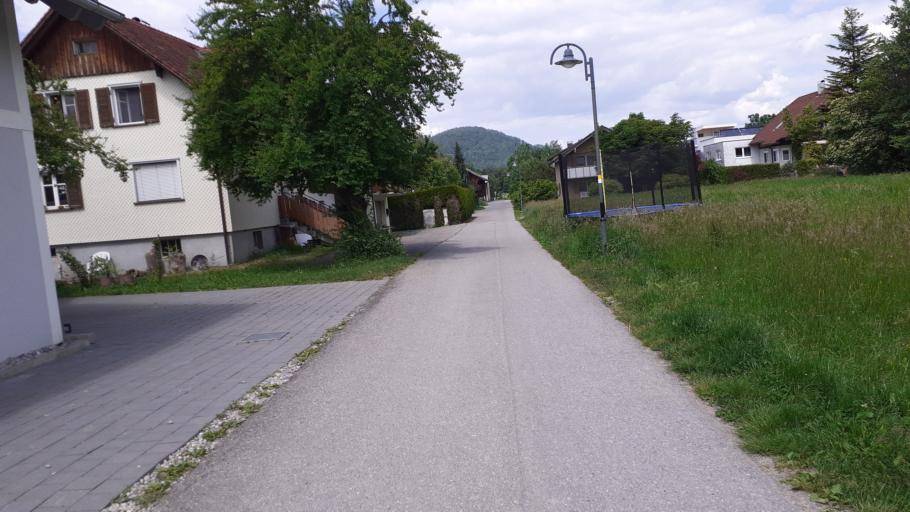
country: AT
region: Vorarlberg
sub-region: Politischer Bezirk Feldkirch
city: Koblach
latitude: 47.3112
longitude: 9.6115
